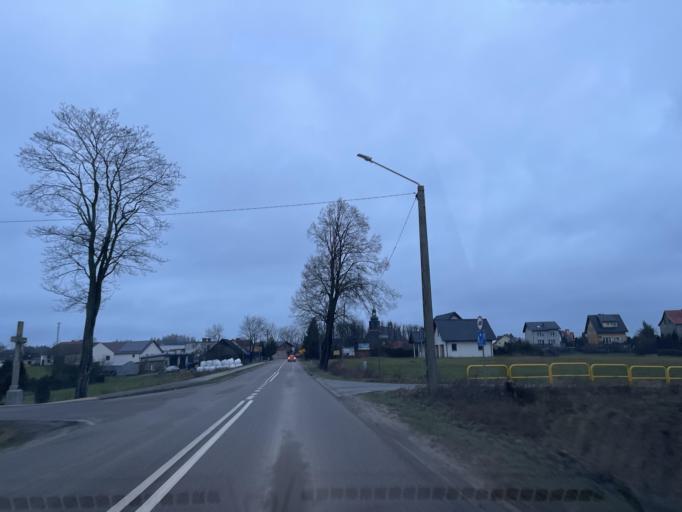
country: PL
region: Pomeranian Voivodeship
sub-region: Powiat wejherowski
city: Szemud
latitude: 54.4133
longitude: 18.2037
